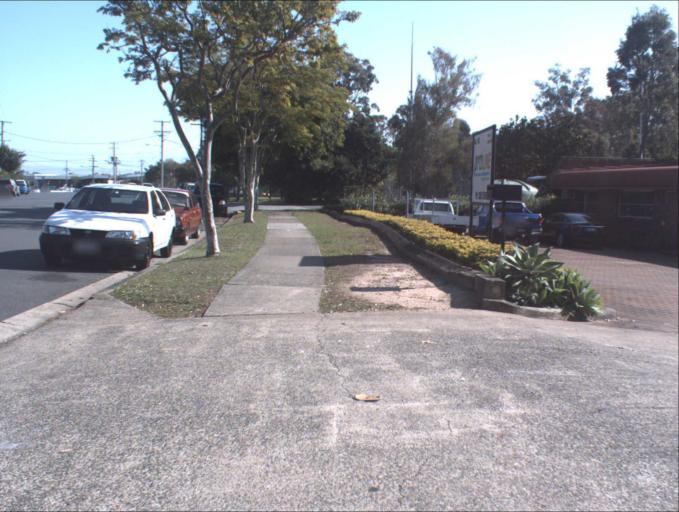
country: AU
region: Queensland
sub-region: Logan
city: Logan Reserve
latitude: -27.6784
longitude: 153.0786
